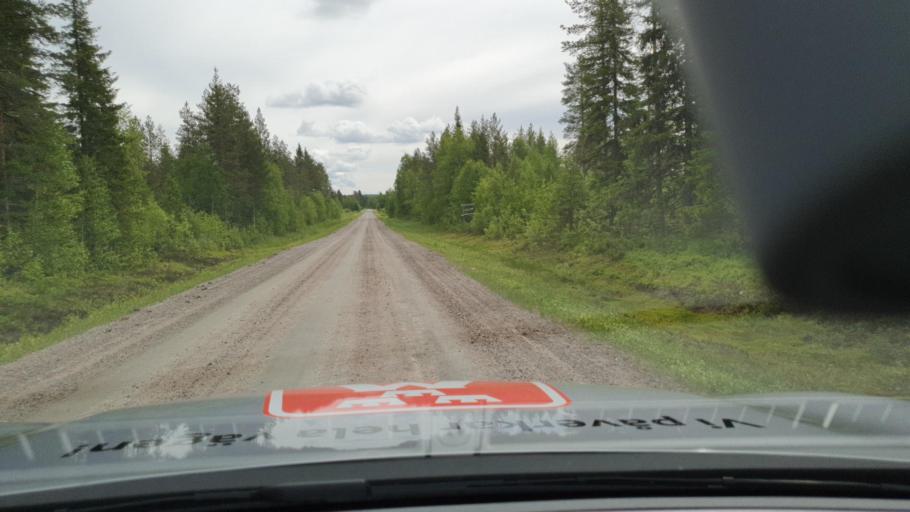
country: FI
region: Lapland
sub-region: Torniolaakso
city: Ylitornio
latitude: 65.9500
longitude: 23.7797
